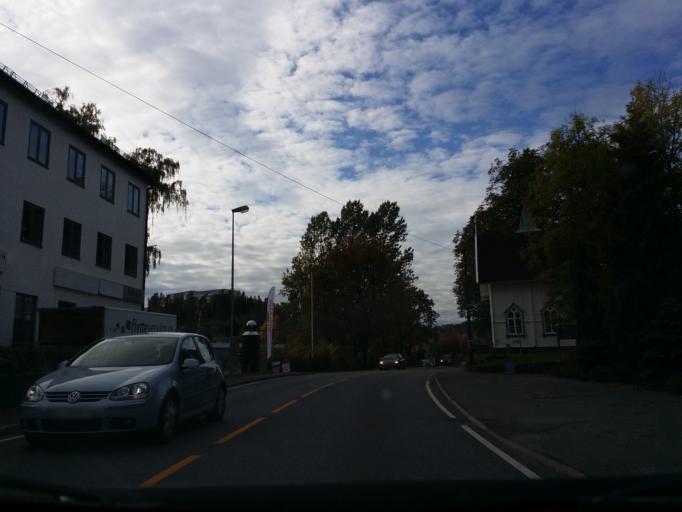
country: NO
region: Akershus
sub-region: Baerum
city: Sandvika
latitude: 59.8921
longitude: 10.5194
